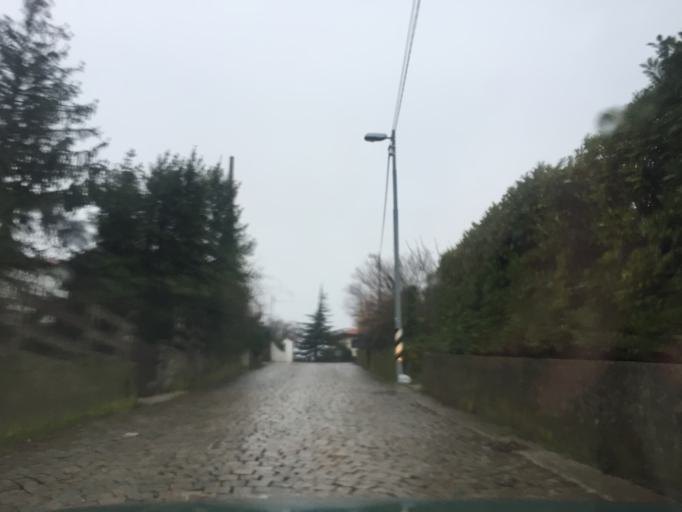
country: IT
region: Friuli Venezia Giulia
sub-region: Provincia di Trieste
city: Muggia
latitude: 45.6012
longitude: 13.7556
